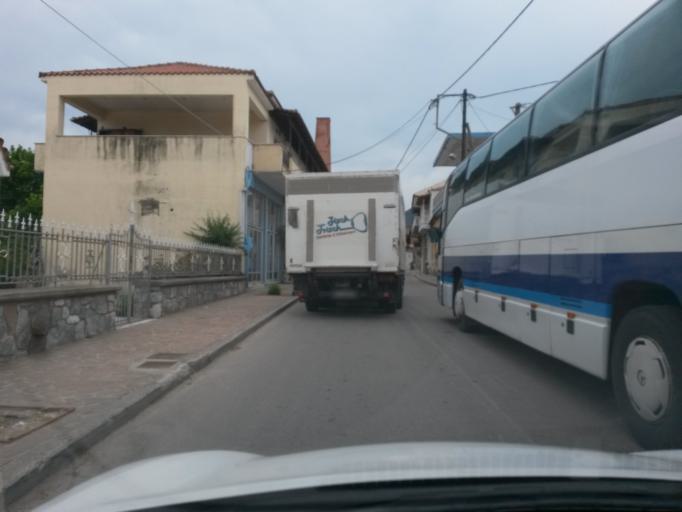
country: GR
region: North Aegean
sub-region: Nomos Lesvou
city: Pappados
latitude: 39.0416
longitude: 26.4561
